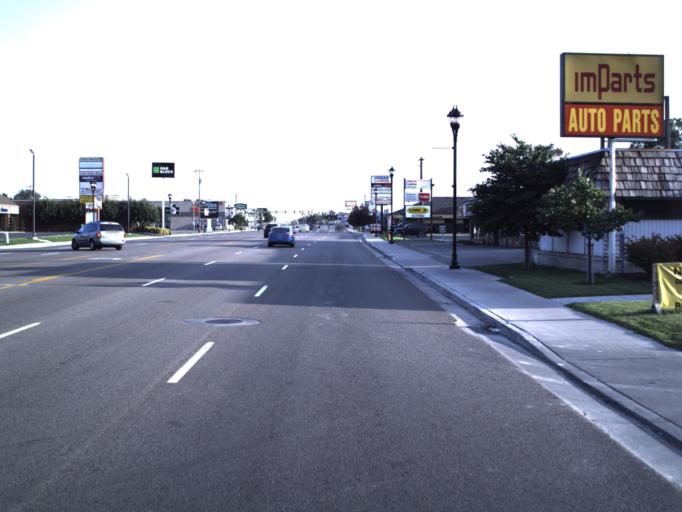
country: US
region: Utah
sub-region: Salt Lake County
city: Midvale
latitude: 40.6243
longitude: -111.8904
